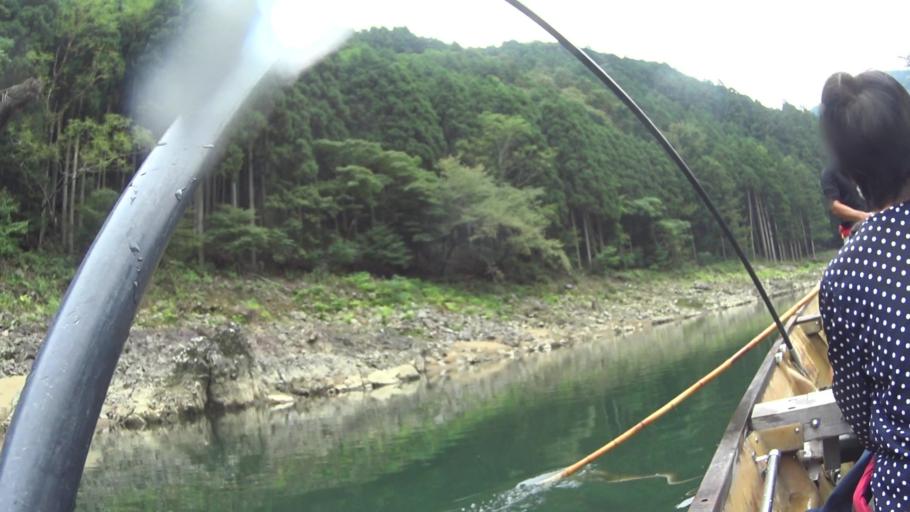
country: JP
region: Kyoto
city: Kameoka
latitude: 35.0219
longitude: 135.6324
